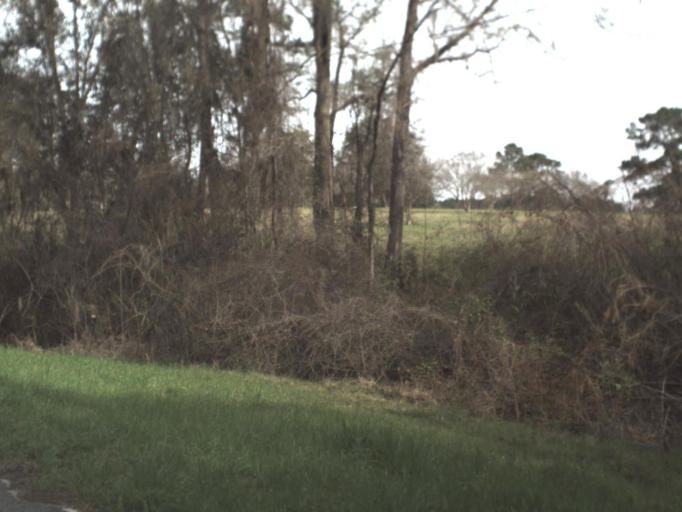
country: US
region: Florida
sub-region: Jefferson County
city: Monticello
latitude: 30.5340
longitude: -83.9471
